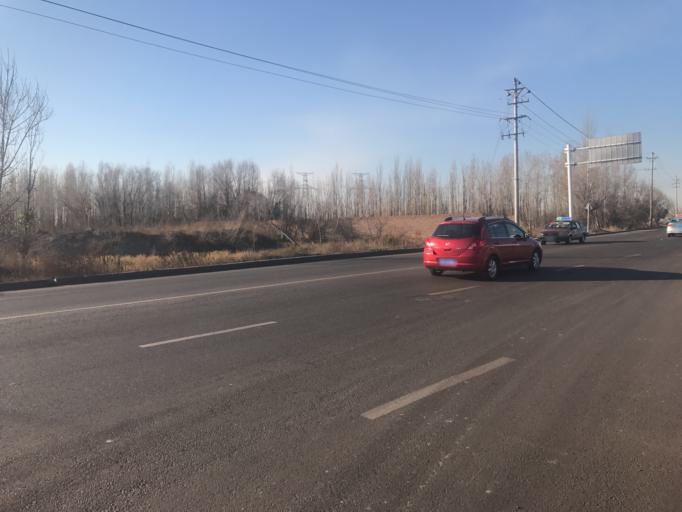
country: CN
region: Xinjiang Uygur Zizhiqu
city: Yengiyar
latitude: 43.9236
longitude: 81.2216
